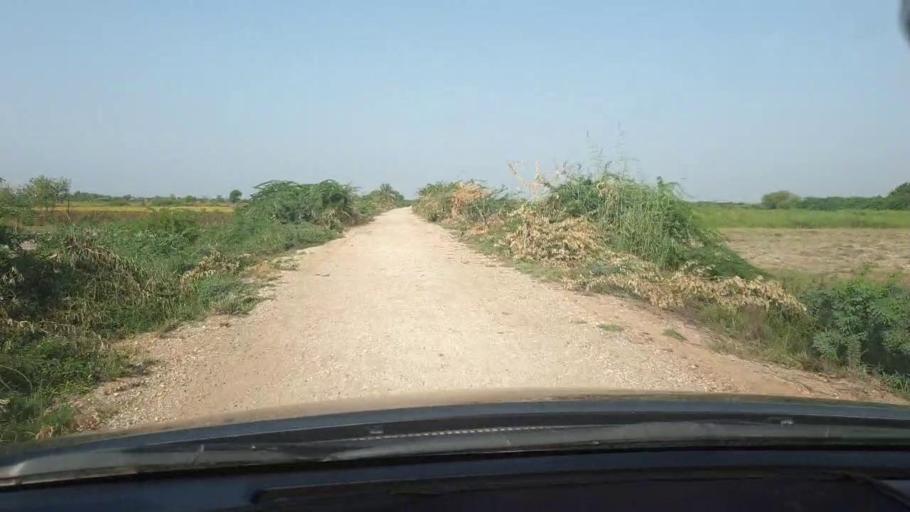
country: PK
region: Sindh
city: Tando Bago
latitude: 24.6799
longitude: 69.1570
